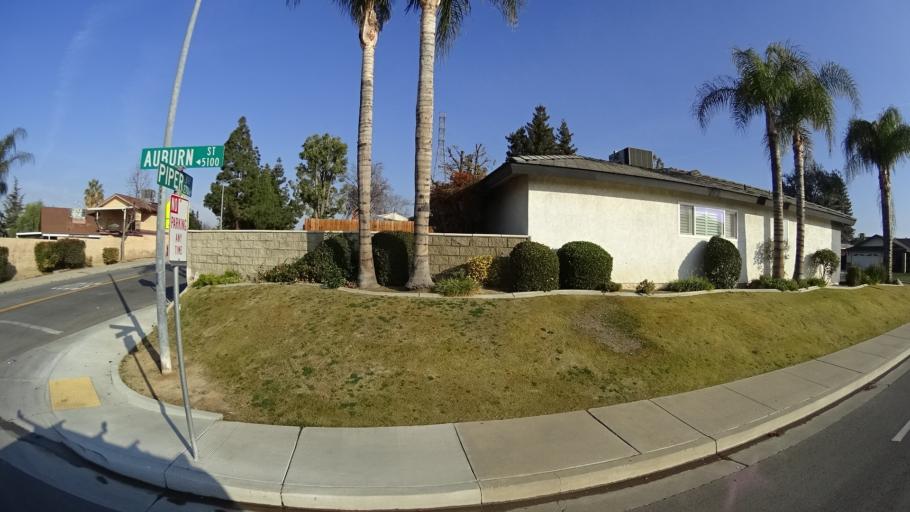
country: US
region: California
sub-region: Kern County
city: Bakersfield
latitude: 35.3979
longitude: -118.9364
